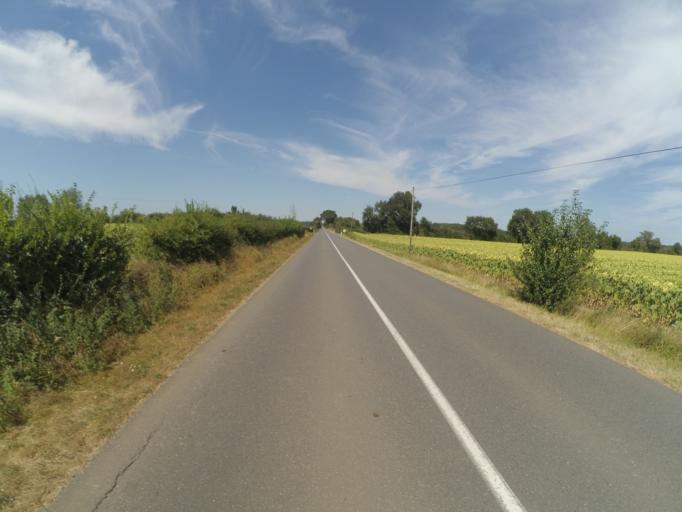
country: FR
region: Poitou-Charentes
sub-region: Departement de la Vienne
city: Usson-du-Poitou
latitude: 46.2564
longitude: 0.5235
